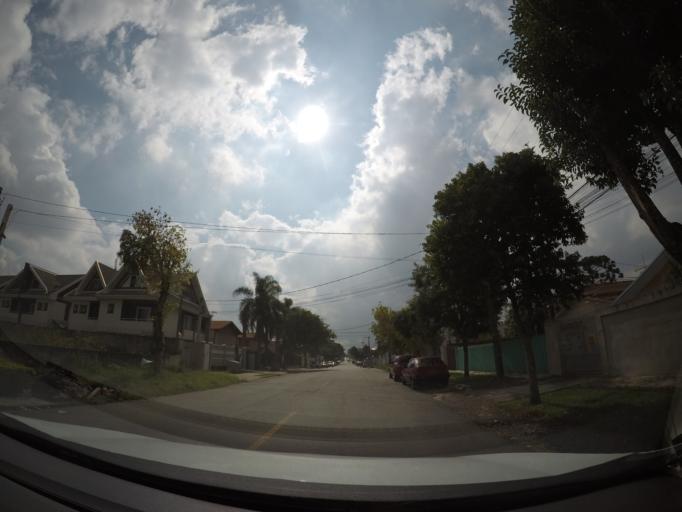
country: BR
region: Parana
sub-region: Sao Jose Dos Pinhais
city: Sao Jose dos Pinhais
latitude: -25.4872
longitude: -49.2485
